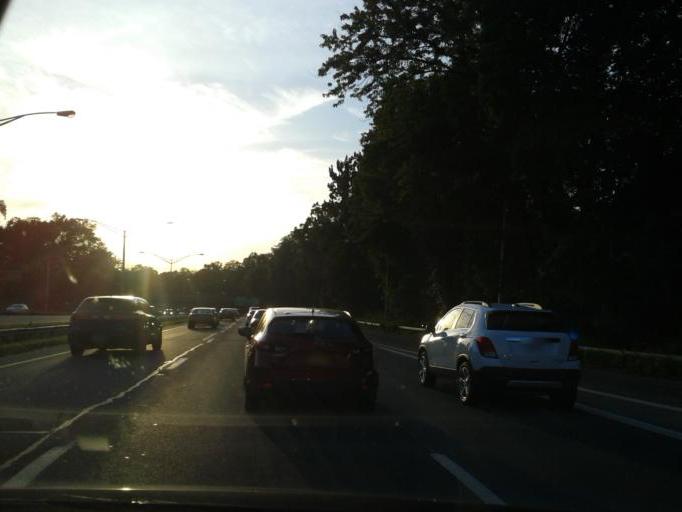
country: US
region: New York
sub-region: Westchester County
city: Bronxville
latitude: 40.9244
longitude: -73.8257
